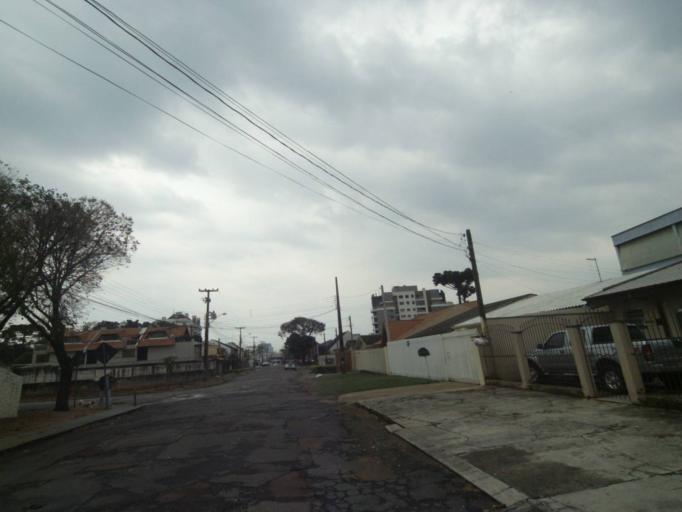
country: BR
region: Parana
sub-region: Curitiba
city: Curitiba
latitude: -25.4726
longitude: -49.2987
